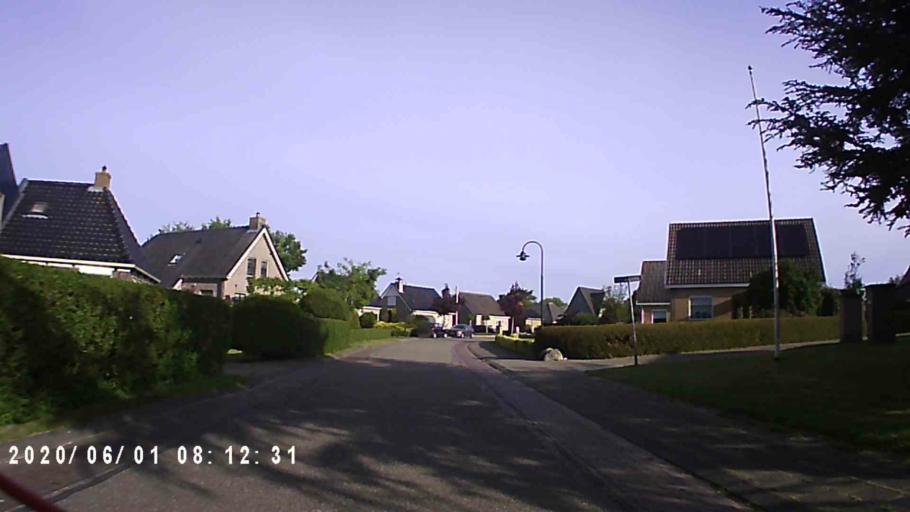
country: NL
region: Friesland
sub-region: Gemeente Ferwerderadiel
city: Burdaard
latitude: 53.2928
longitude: 5.8807
